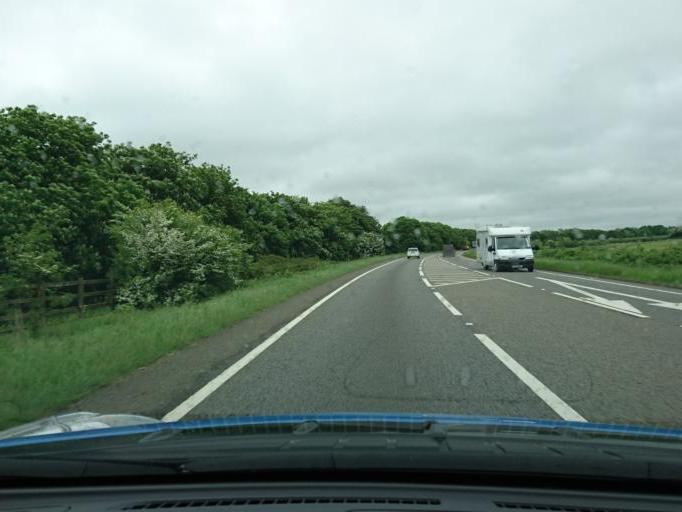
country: GB
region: England
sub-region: Oxfordshire
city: Faringdon
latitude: 51.6430
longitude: -1.5991
